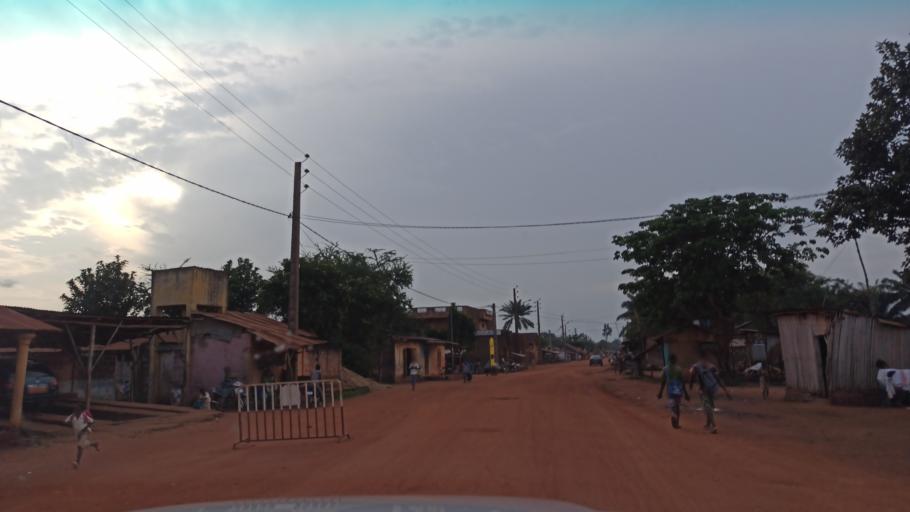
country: BJ
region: Queme
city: Porto-Novo
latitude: 6.5327
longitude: 2.6615
